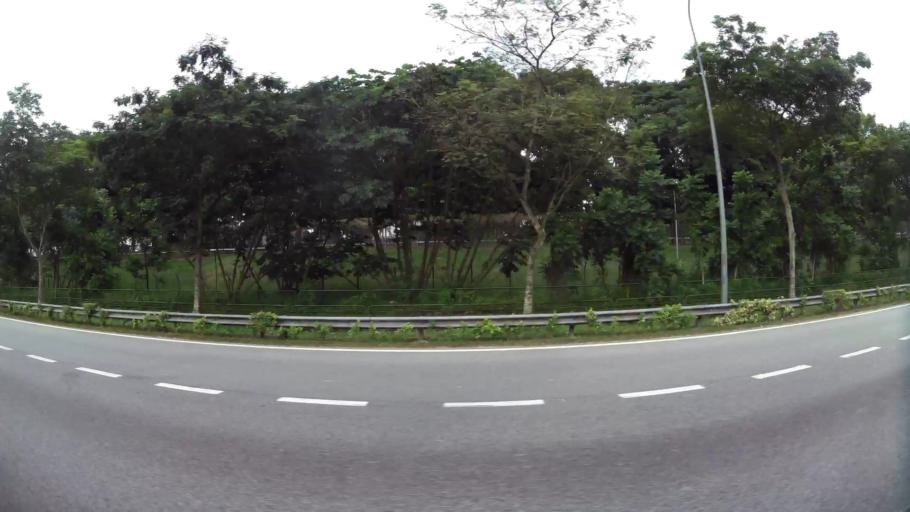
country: MY
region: Johor
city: Johor Bahru
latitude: 1.4203
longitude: 103.7991
